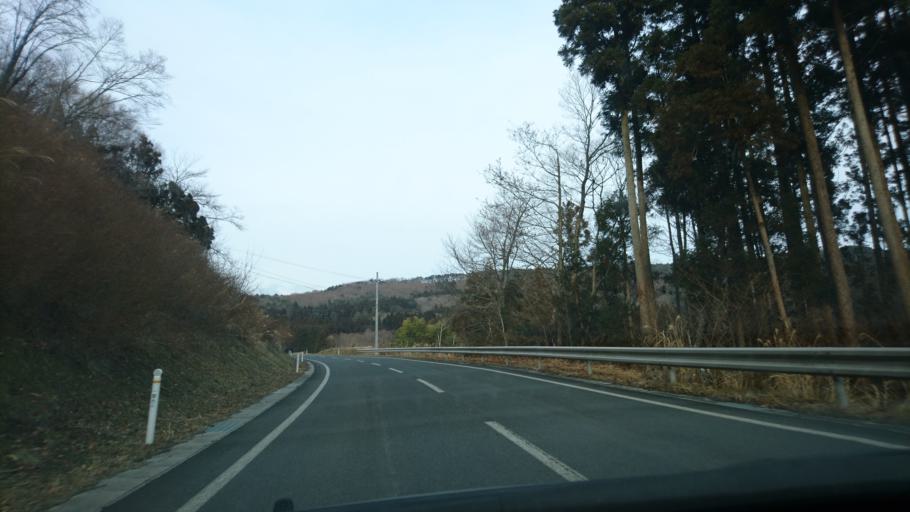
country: JP
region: Iwate
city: Ichinoseki
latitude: 38.8557
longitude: 141.3906
